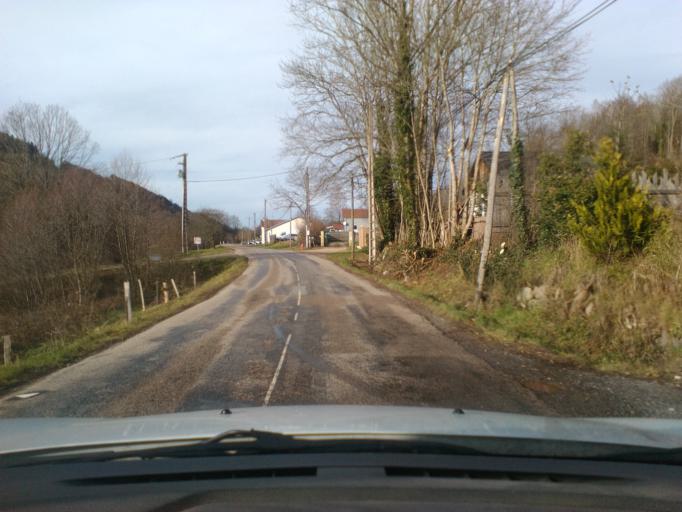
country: FR
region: Lorraine
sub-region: Departement des Vosges
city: Fraize
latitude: 48.1633
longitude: 6.9842
